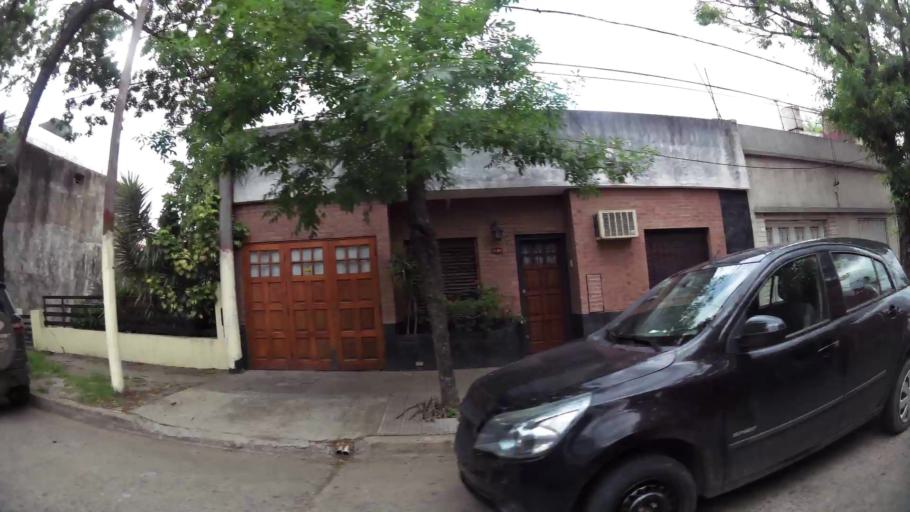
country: AR
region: Santa Fe
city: Gobernador Galvez
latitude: -33.0007
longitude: -60.6504
